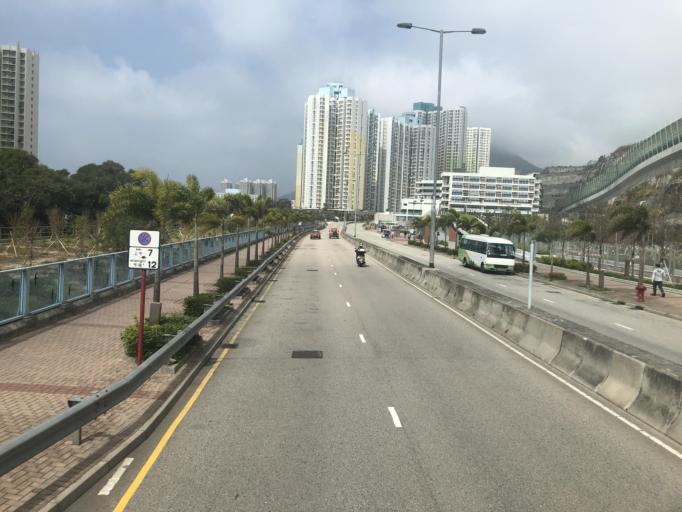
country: HK
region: Kowloon City
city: Kowloon
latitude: 22.3221
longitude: 114.2325
